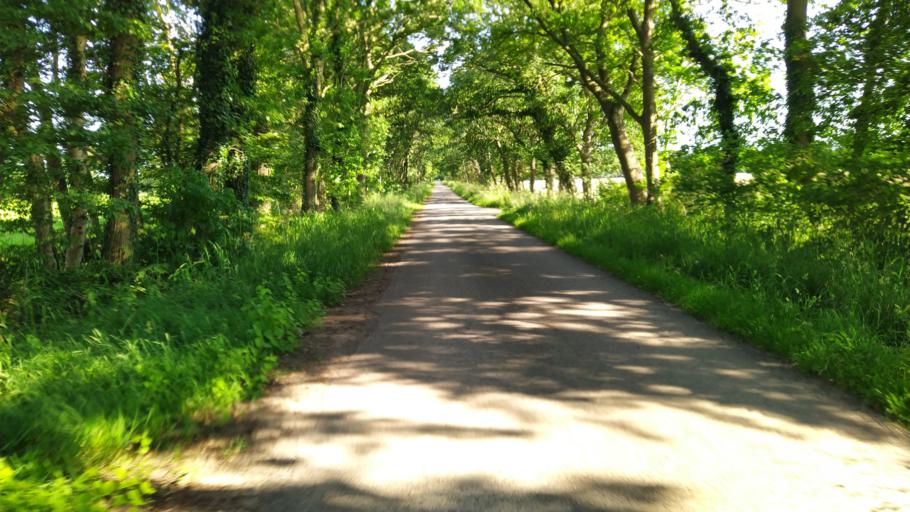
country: DE
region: Lower Saxony
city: Lintig
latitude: 53.6137
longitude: 8.8878
